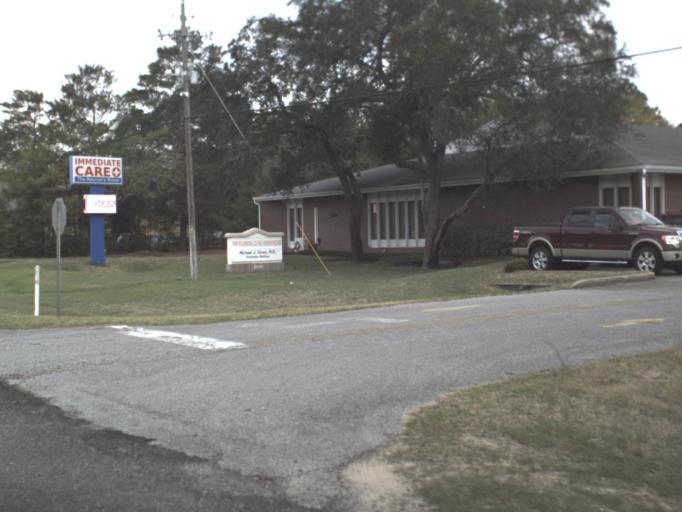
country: US
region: Florida
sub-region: Okaloosa County
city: Ocean City
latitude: 30.4696
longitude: -86.6083
